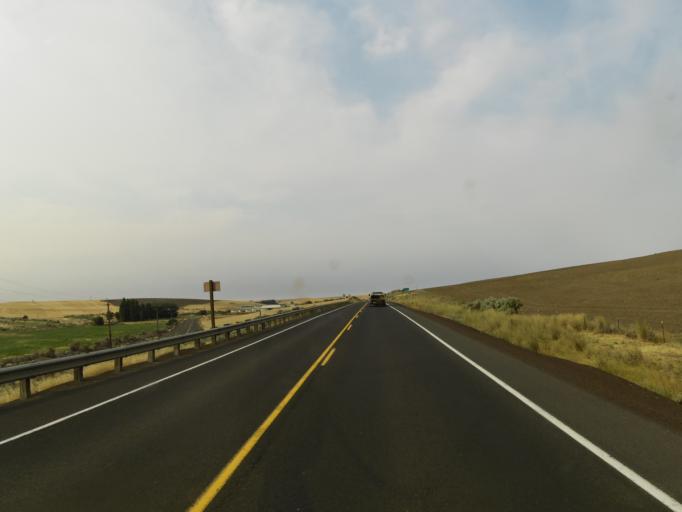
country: US
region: Oregon
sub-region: Sherman County
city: Moro
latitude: 45.4800
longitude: -120.7375
